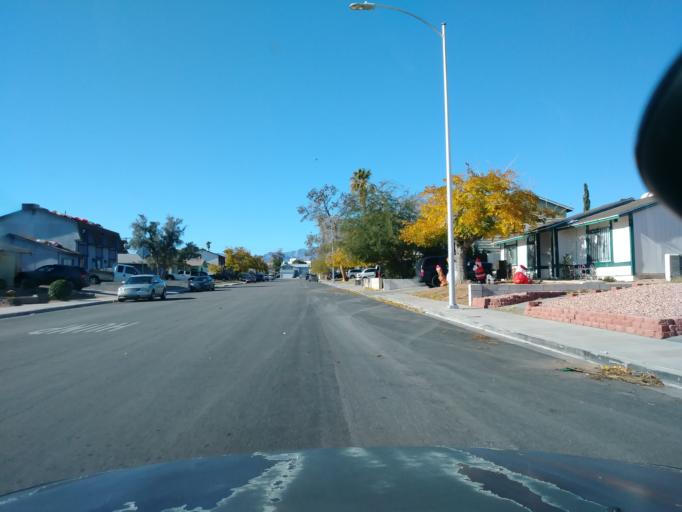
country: US
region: Nevada
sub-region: Clark County
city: Spring Valley
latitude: 36.1778
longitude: -115.2352
